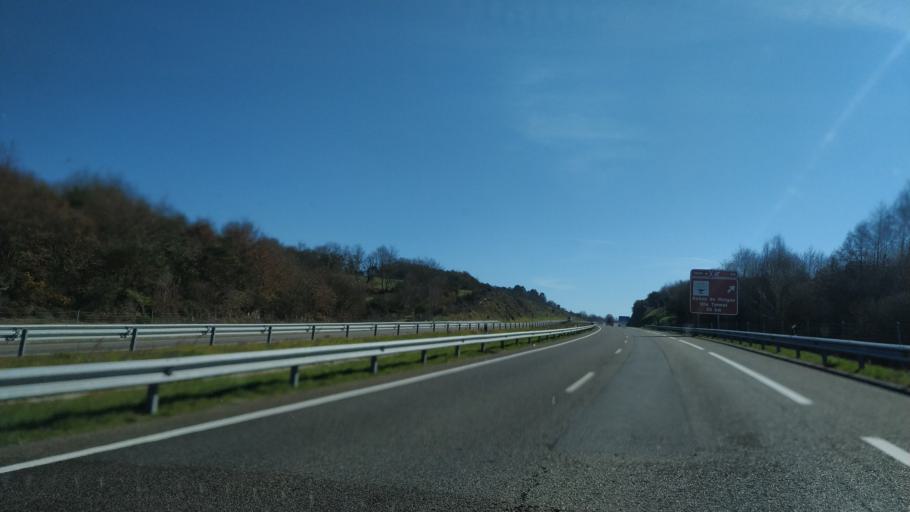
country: ES
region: Galicia
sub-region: Provincia de Ourense
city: Taboadela
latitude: 42.2163
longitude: -7.8405
